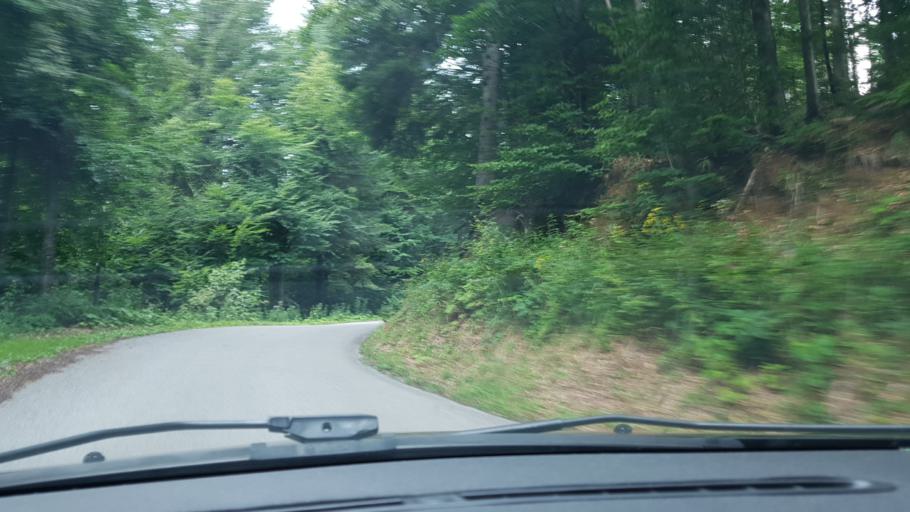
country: HR
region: Primorsko-Goranska
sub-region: Grad Delnice
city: Delnice
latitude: 45.3805
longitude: 14.6942
